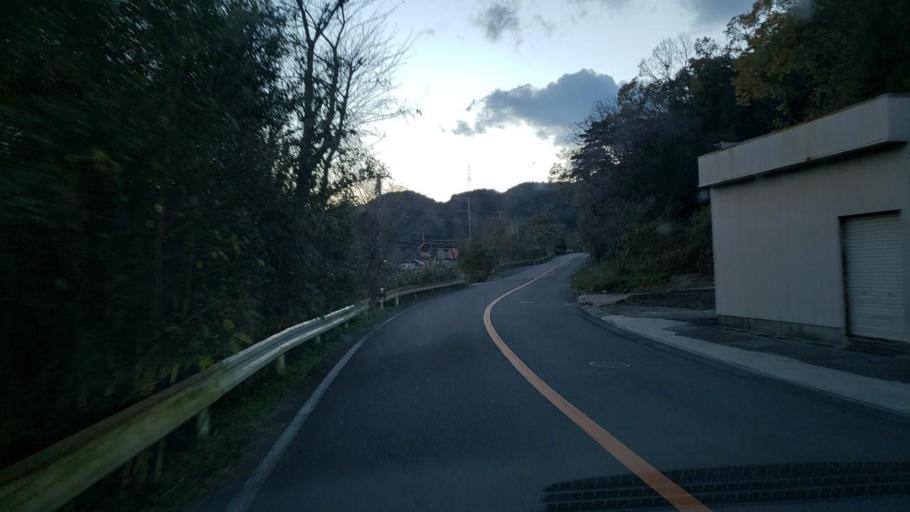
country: JP
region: Hyogo
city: Fukura
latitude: 34.2909
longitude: 134.7206
